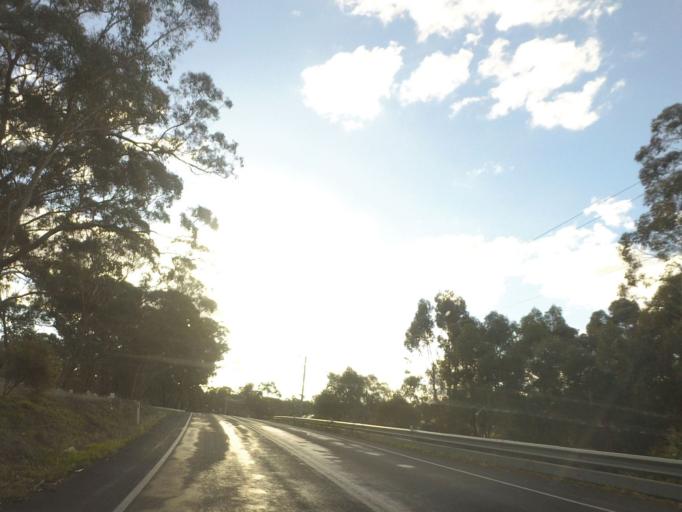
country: AU
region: Victoria
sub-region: Mount Alexander
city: Castlemaine
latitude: -37.0906
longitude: 144.2845
